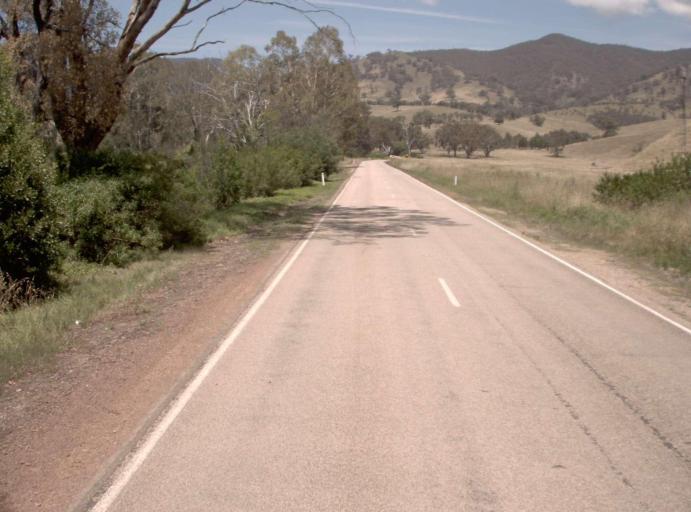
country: AU
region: Victoria
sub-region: East Gippsland
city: Bairnsdale
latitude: -37.2809
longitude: 147.7404
